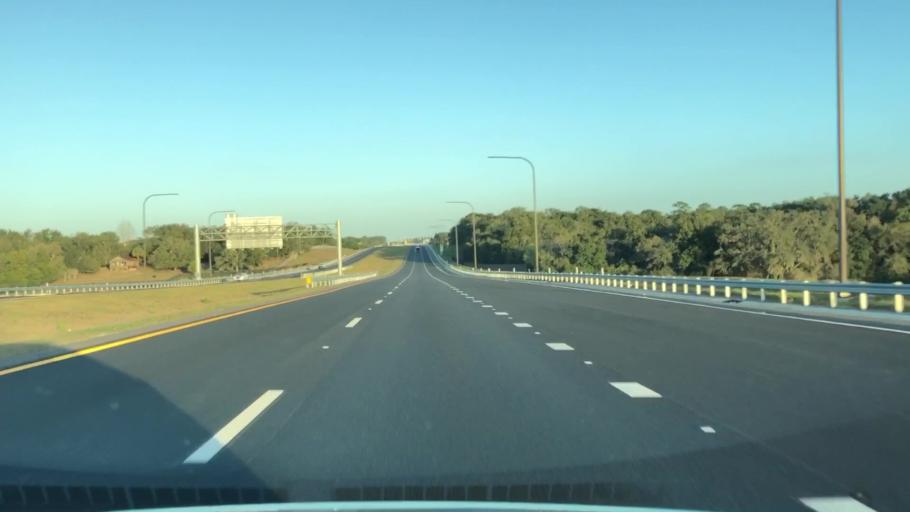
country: US
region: Florida
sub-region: Lake County
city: Mount Plymouth
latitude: 28.7755
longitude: -81.5527
